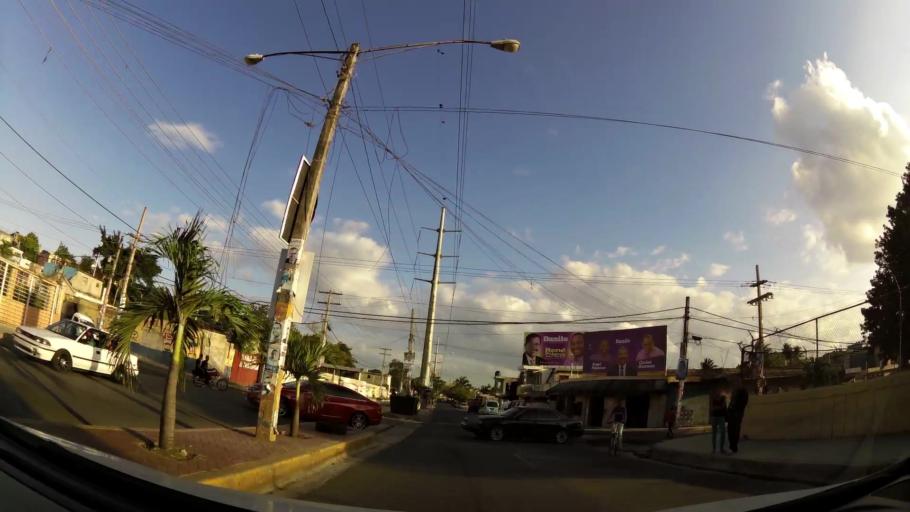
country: DO
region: Nacional
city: La Agustina
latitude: 18.5407
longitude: -69.9274
